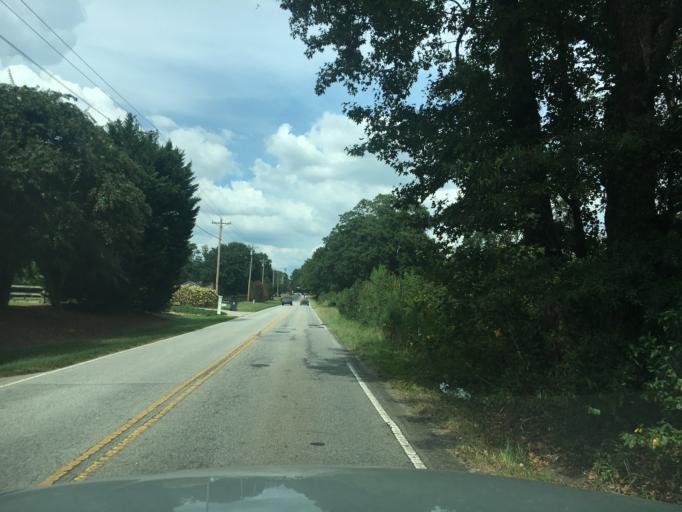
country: US
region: South Carolina
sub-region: Greenville County
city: Five Forks
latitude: 34.8186
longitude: -82.2289
